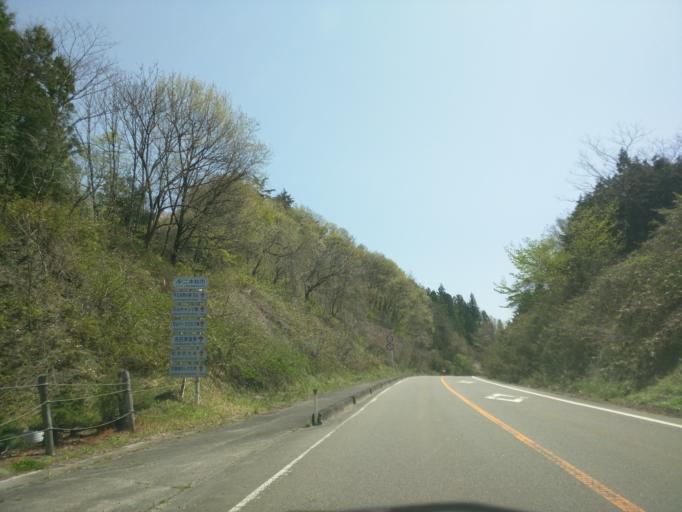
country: JP
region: Fukushima
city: Nihommatsu
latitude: 37.5551
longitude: 140.5203
